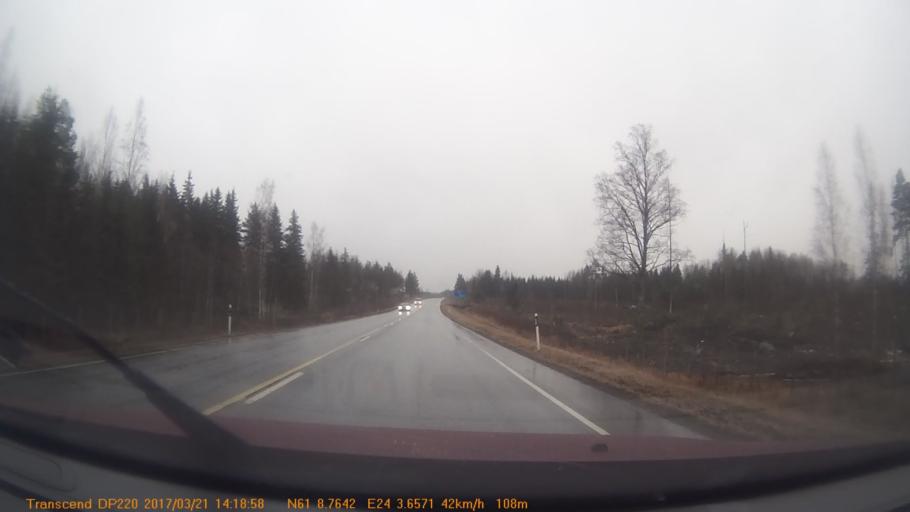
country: FI
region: Haeme
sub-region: Haemeenlinna
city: Kalvola
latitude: 61.1462
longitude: 24.0609
